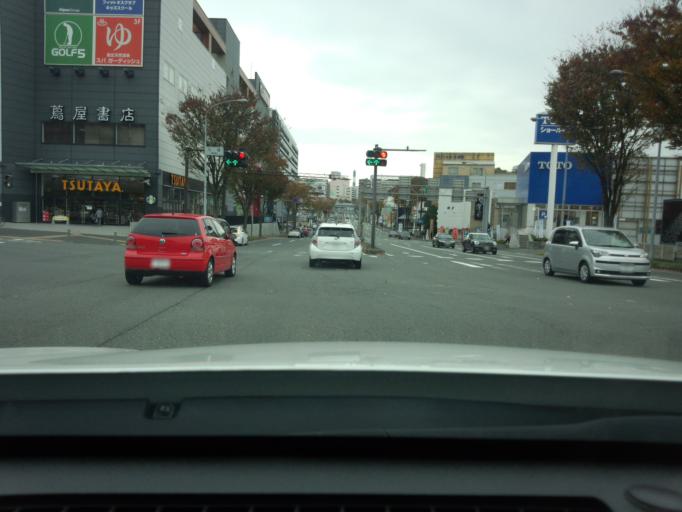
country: JP
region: Tokyo
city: Chofugaoka
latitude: 35.5518
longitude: 139.5754
